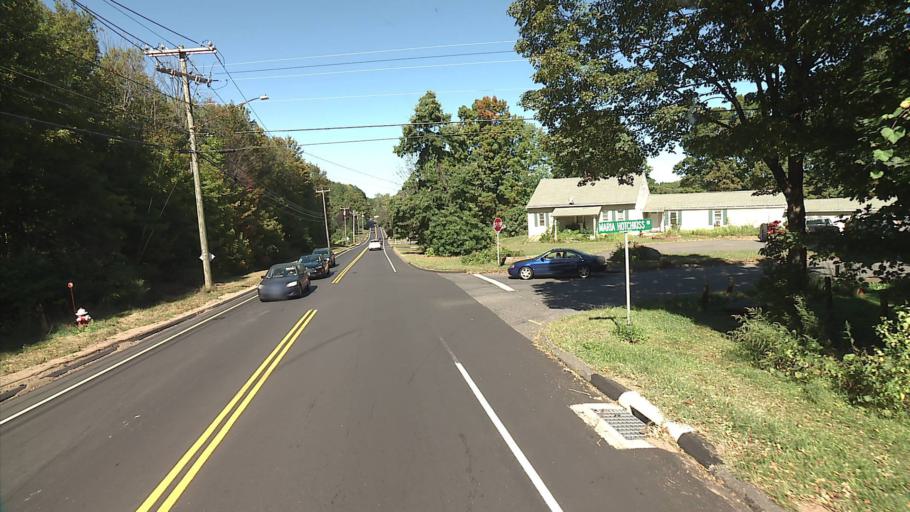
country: US
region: Connecticut
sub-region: New Haven County
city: Prospect
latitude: 41.5217
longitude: -72.9933
